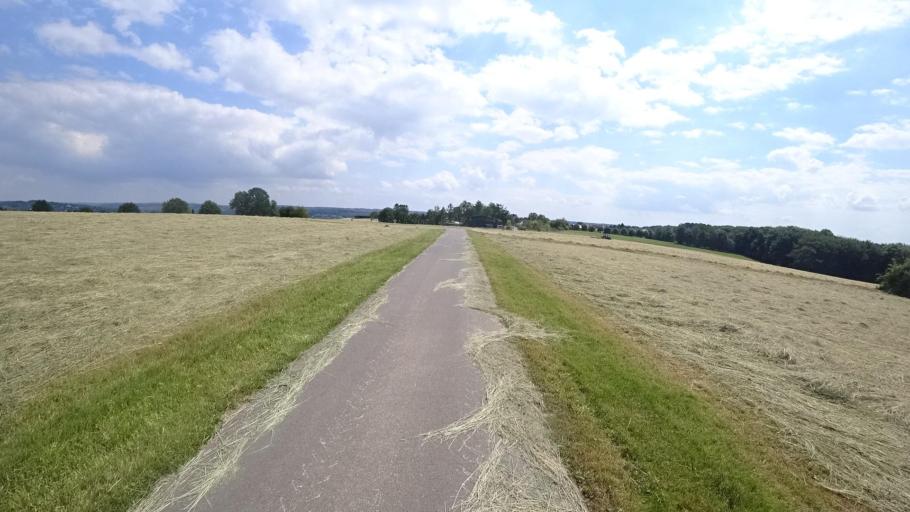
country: DE
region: Rheinland-Pfalz
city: Helmenzen
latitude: 50.7007
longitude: 7.6184
